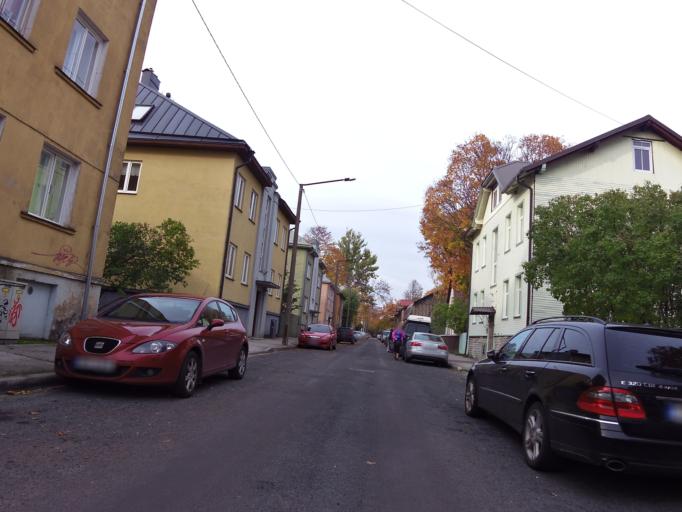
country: EE
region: Harju
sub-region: Tallinna linn
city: Tallinn
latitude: 59.4379
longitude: 24.7152
